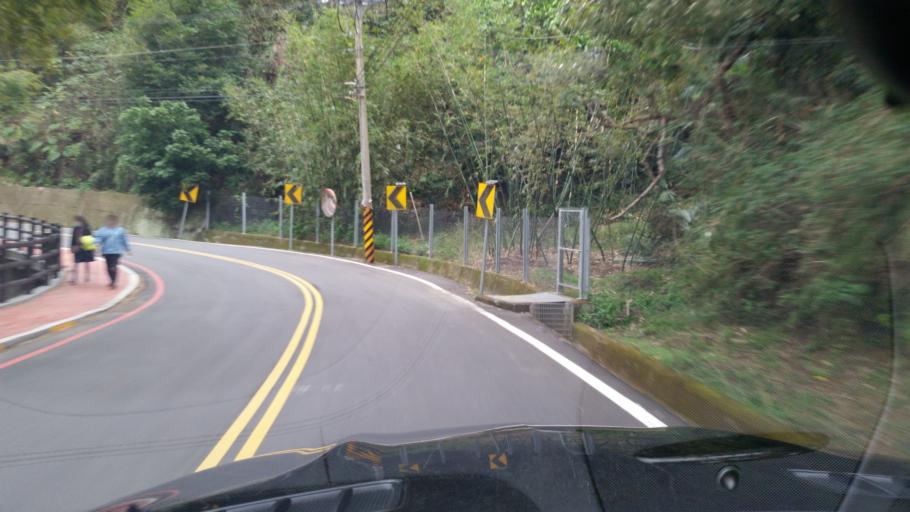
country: TW
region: Taiwan
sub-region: Miaoli
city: Miaoli
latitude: 24.5804
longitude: 120.8834
